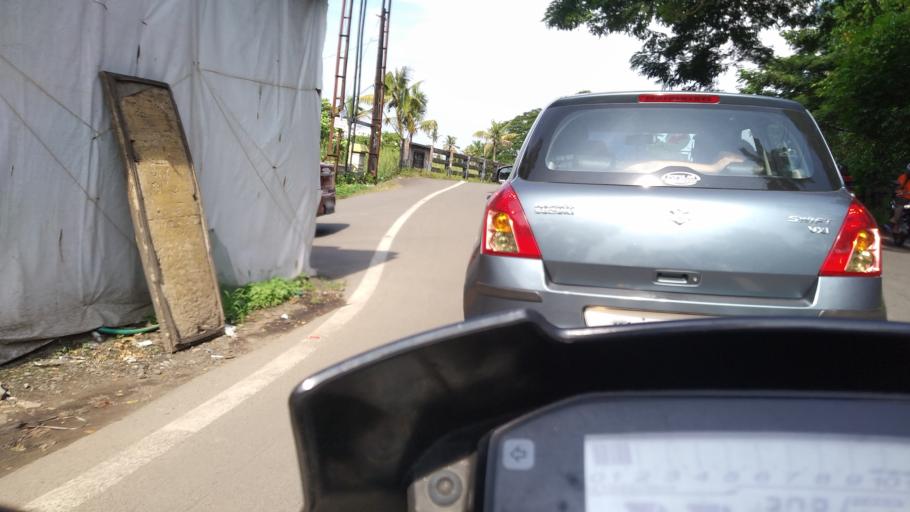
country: IN
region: Kerala
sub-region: Ernakulam
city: Cochin
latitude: 9.9838
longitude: 76.3024
